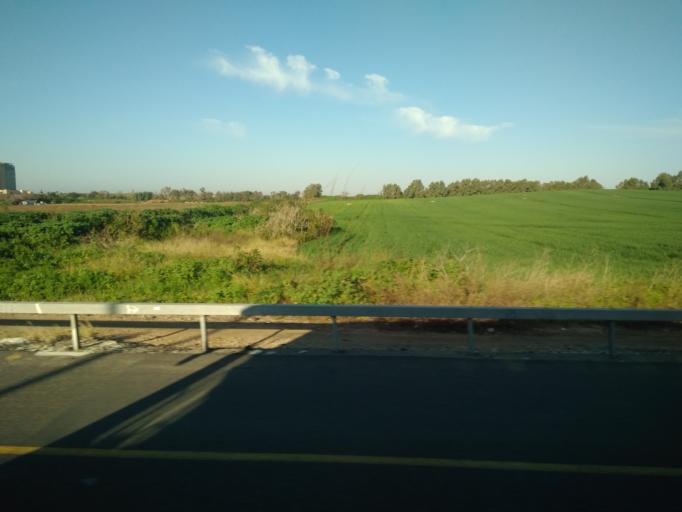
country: IL
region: Tel Aviv
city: Herzliya Pituah
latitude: 32.1464
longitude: 34.8029
